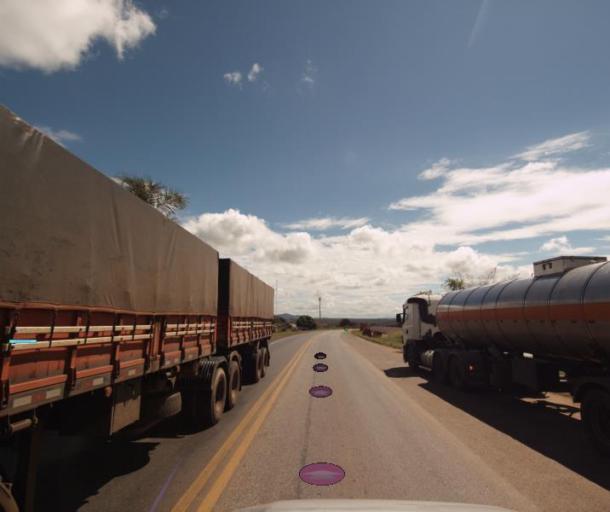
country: BR
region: Goias
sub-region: Uruacu
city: Uruacu
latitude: -14.5259
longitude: -49.1593
